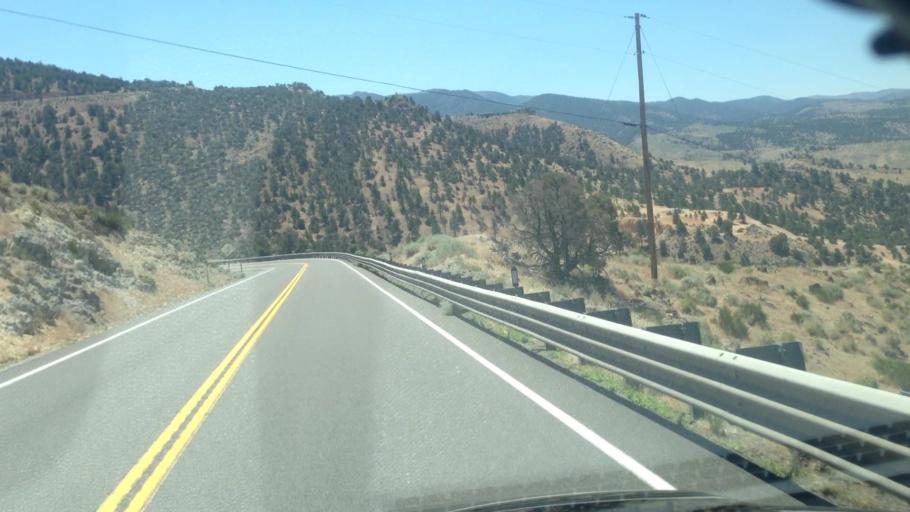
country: US
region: Nevada
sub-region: Storey County
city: Virginia City
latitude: 39.3910
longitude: -119.7105
